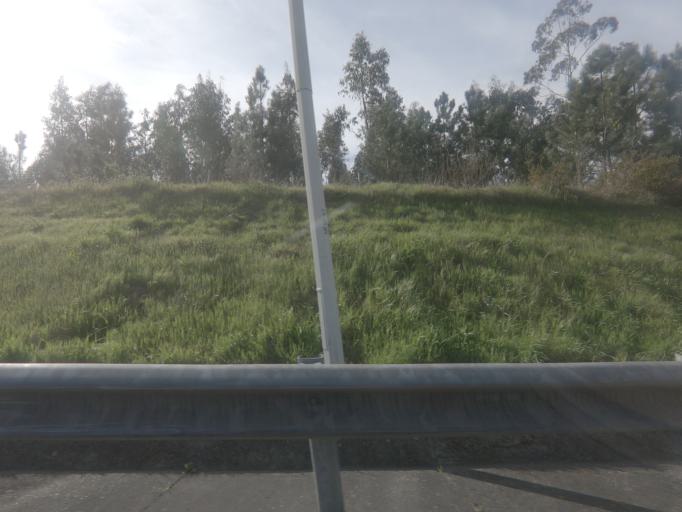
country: PT
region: Leiria
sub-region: Leiria
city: Leiria
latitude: 39.7422
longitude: -8.7690
